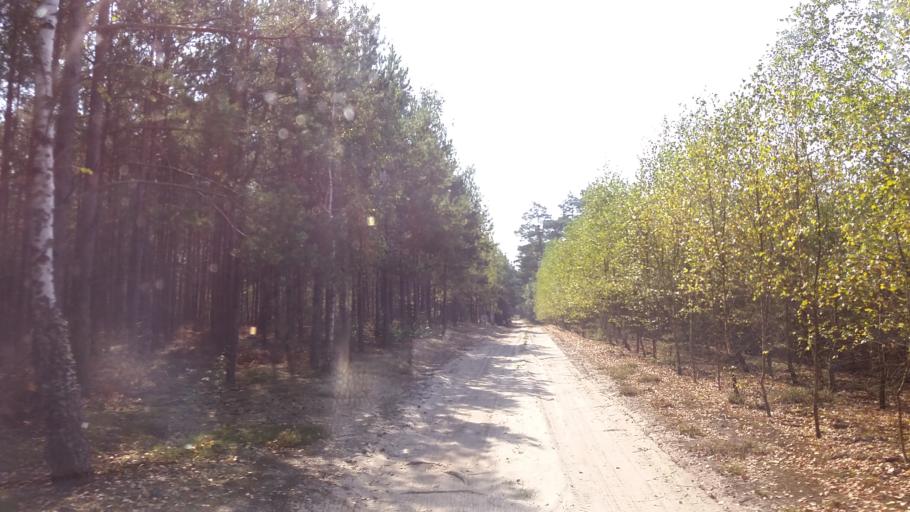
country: PL
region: West Pomeranian Voivodeship
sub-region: Powiat drawski
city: Kalisz Pomorski
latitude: 53.2194
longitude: 15.9028
